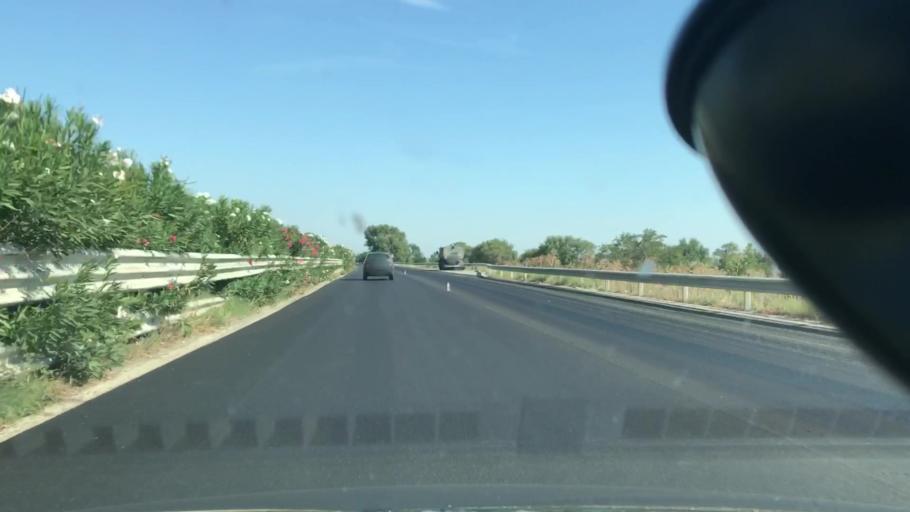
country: IT
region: Apulia
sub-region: Provincia di Foggia
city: Ascoli Satriano
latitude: 41.2712
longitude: 15.5525
